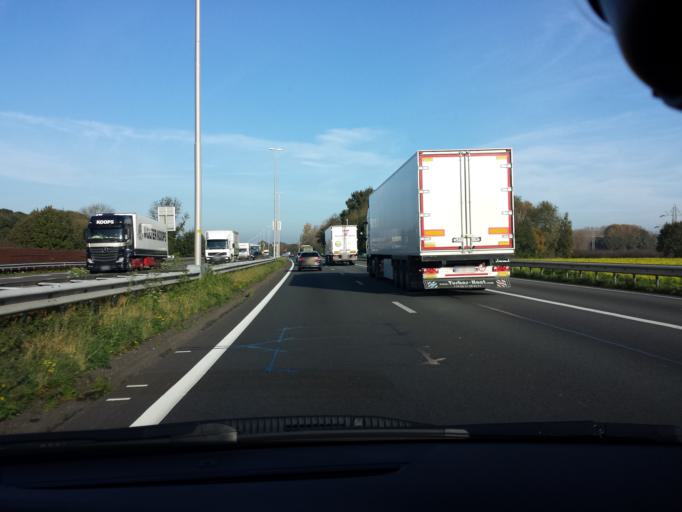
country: NL
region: Limburg
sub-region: Gemeente Sittard-Geleen
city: Born
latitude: 51.0519
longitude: 5.8272
